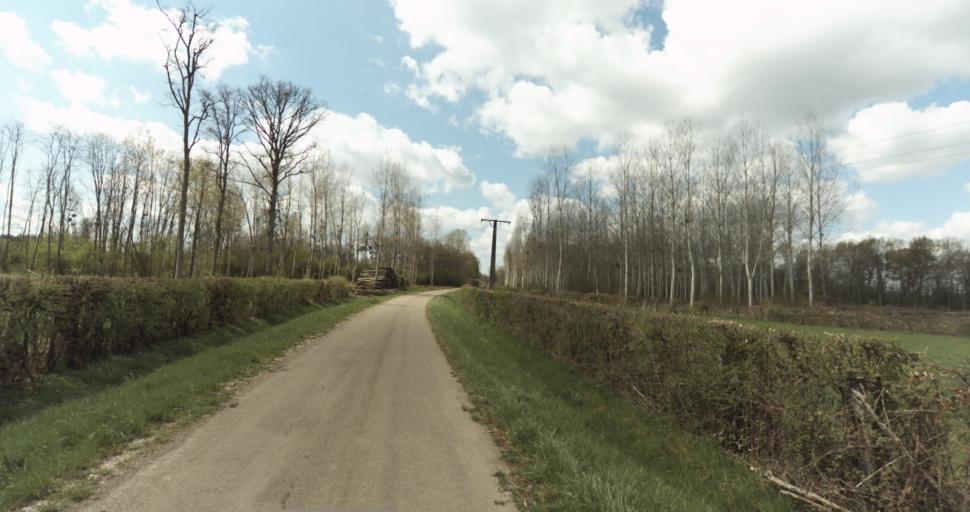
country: FR
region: Bourgogne
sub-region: Departement de la Cote-d'Or
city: Auxonne
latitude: 47.1784
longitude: 5.3672
